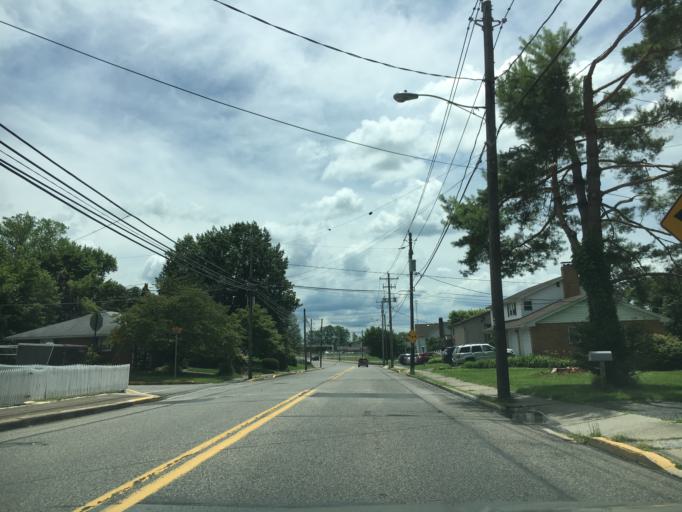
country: US
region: Pennsylvania
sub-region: Lehigh County
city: Cementon
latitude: 40.7005
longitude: -75.5041
